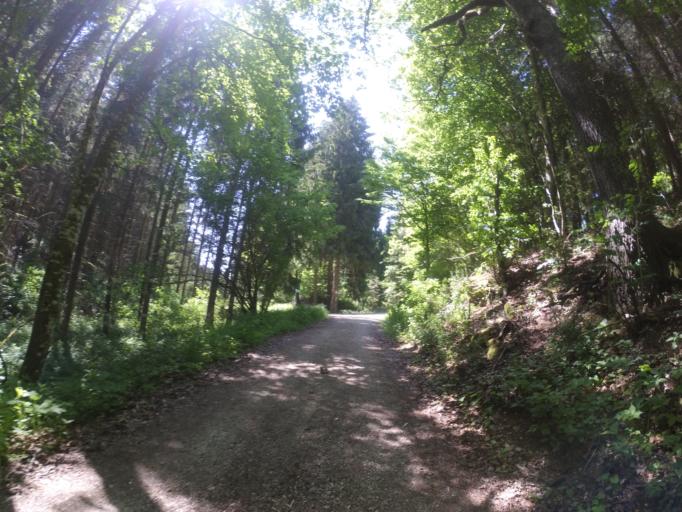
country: DE
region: Baden-Wuerttemberg
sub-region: Tuebingen Region
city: Berghulen
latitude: 48.4879
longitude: 9.7855
